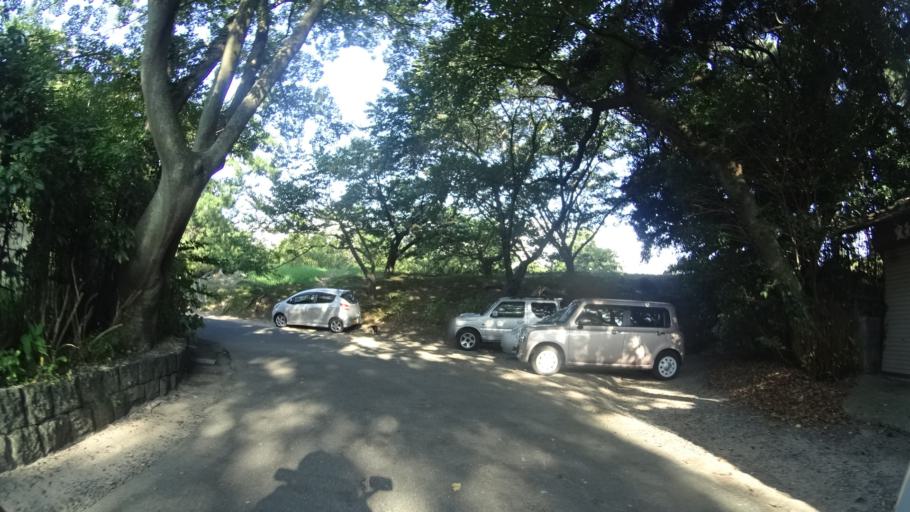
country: JP
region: Yamaguchi
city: Hagi
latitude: 34.4162
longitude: 131.3832
